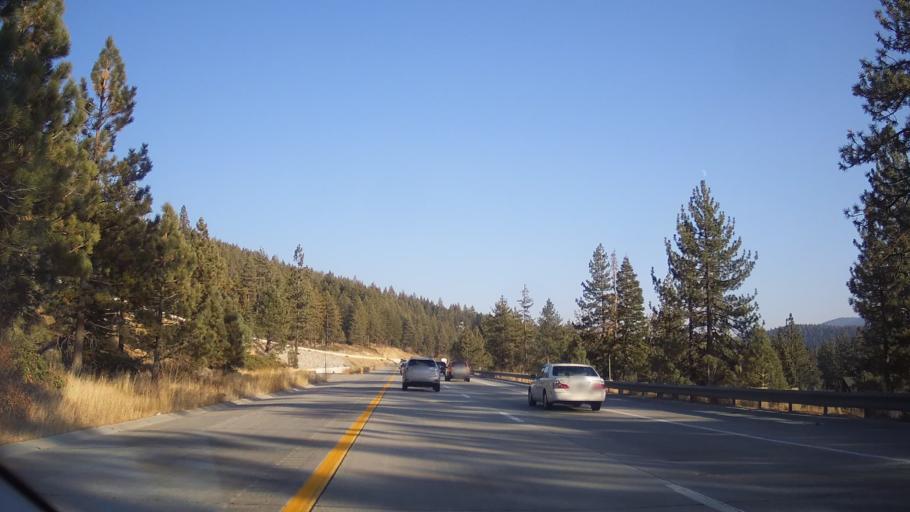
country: US
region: California
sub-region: Nevada County
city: Truckee
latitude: 39.3312
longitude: -120.2510
